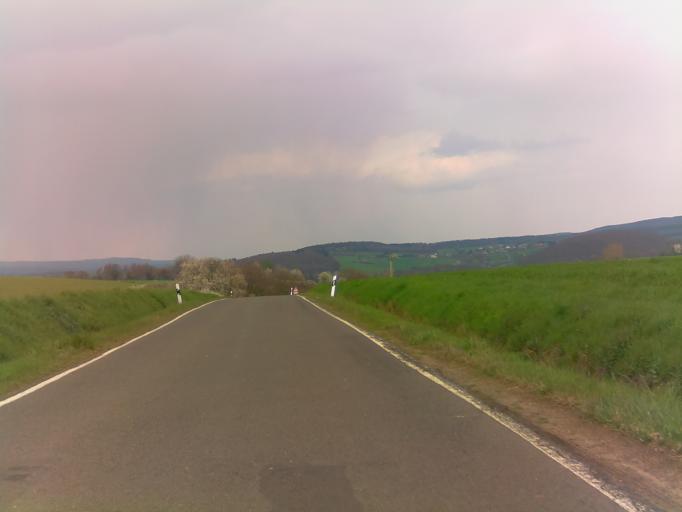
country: DE
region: Rheinland-Pfalz
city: Daubach
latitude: 49.8549
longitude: 7.6289
